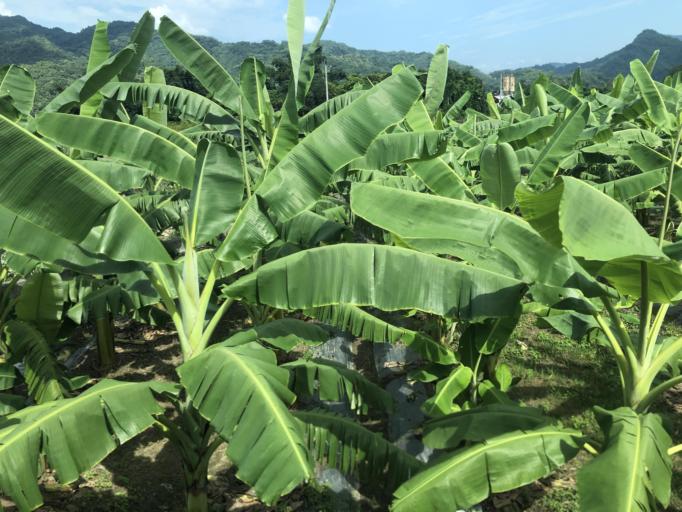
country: TW
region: Taiwan
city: Yujing
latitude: 22.9135
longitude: 120.5700
